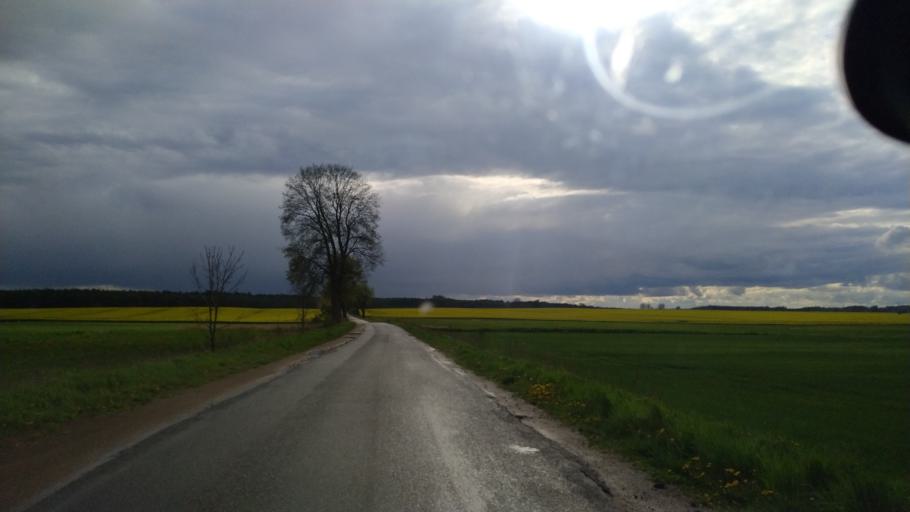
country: PL
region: Pomeranian Voivodeship
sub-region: Powiat starogardzki
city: Smetowo Graniczne
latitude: 53.7173
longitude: 18.6090
